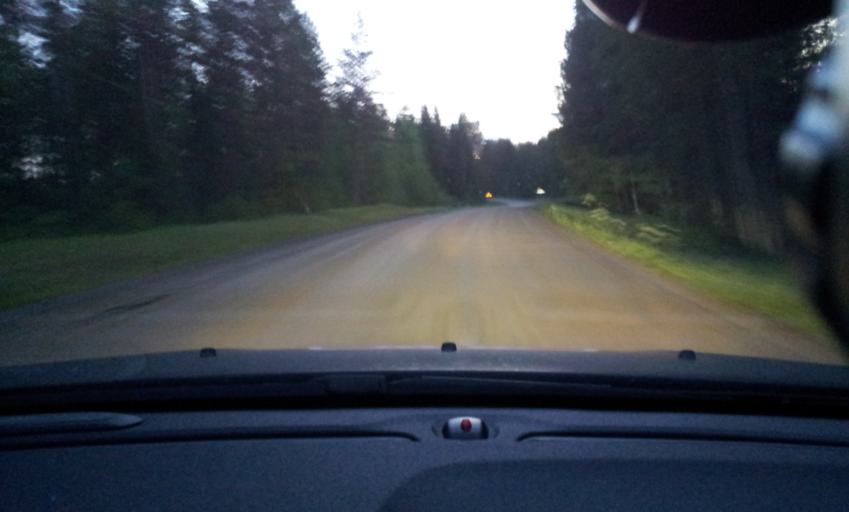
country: SE
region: Jaemtland
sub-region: Braecke Kommun
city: Braecke
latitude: 62.7262
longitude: 15.5012
